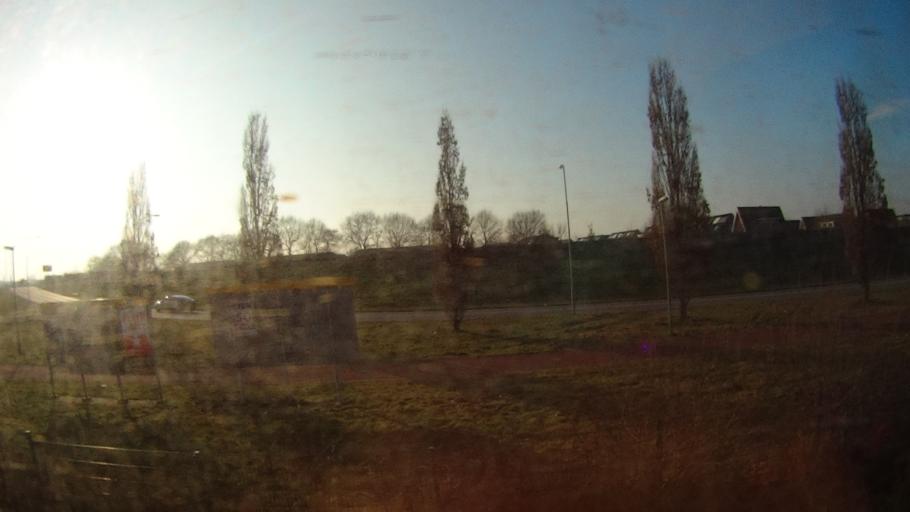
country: NL
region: Gelderland
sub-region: Gemeente Harderwijk
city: Harderwijk
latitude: 52.3259
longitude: 5.6122
